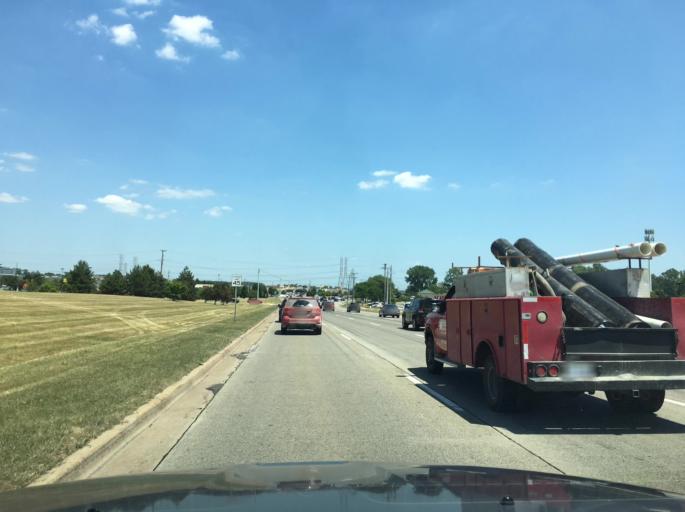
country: US
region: Michigan
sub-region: Macomb County
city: Utica
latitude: 42.6259
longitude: -83.0098
